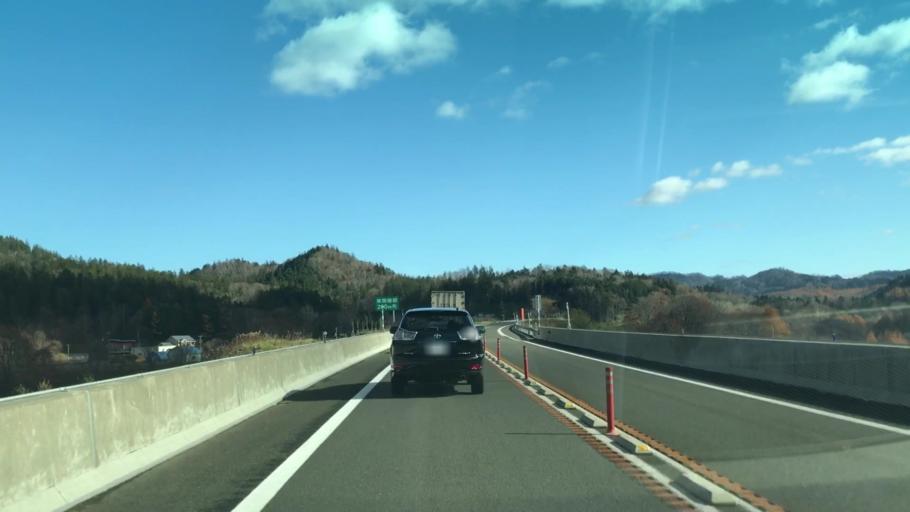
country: JP
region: Hokkaido
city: Iwamizawa
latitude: 42.9330
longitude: 142.0508
